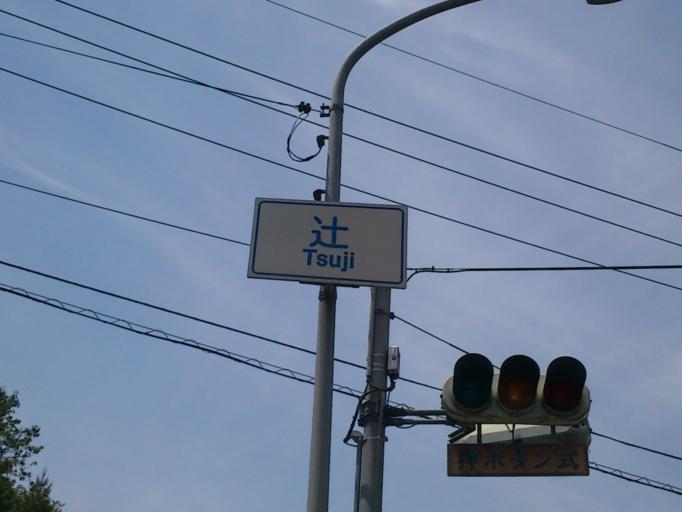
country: JP
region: Kyoto
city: Ayabe
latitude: 35.2145
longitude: 135.2373
